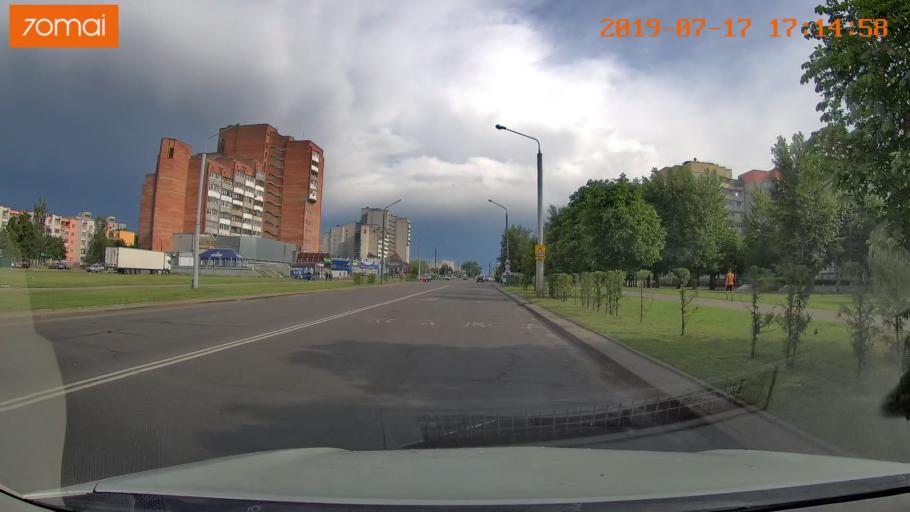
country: BY
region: Mogilev
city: Babruysk
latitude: 53.1725
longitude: 29.1894
